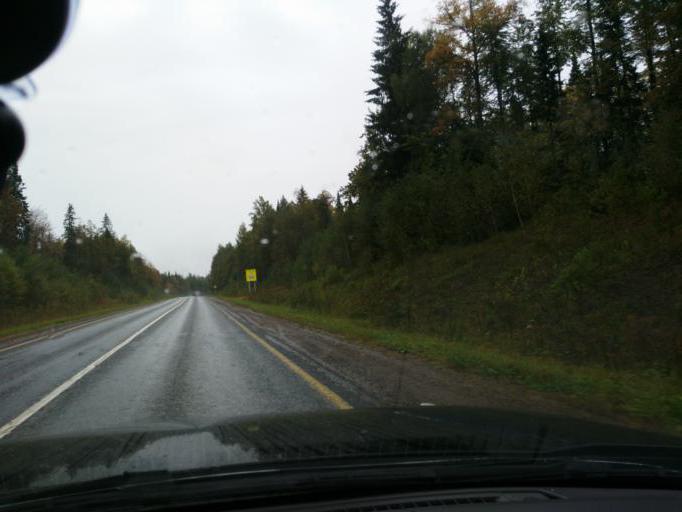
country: RU
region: Perm
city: Yugo-Kamskiy
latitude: 57.5952
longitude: 55.6606
